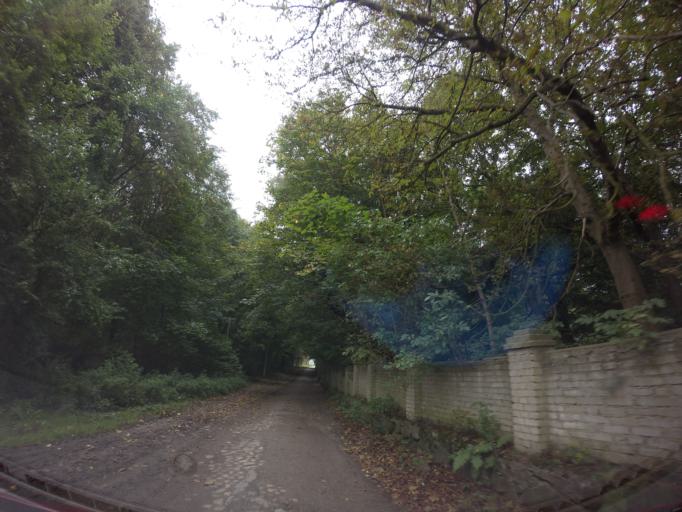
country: PL
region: West Pomeranian Voivodeship
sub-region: Powiat choszczenski
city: Krzecin
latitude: 53.0322
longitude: 15.4556
